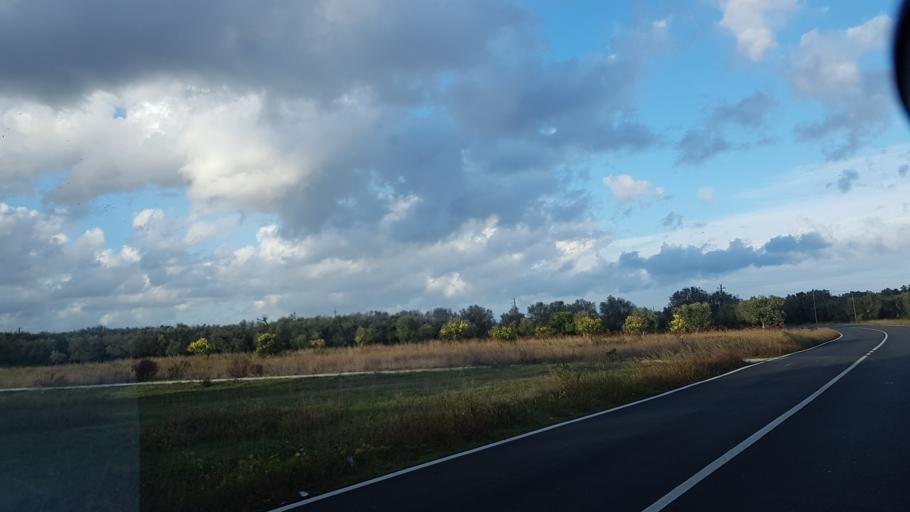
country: IT
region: Apulia
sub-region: Provincia di Brindisi
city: San Pietro Vernotico
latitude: 40.5042
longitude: 18.0072
